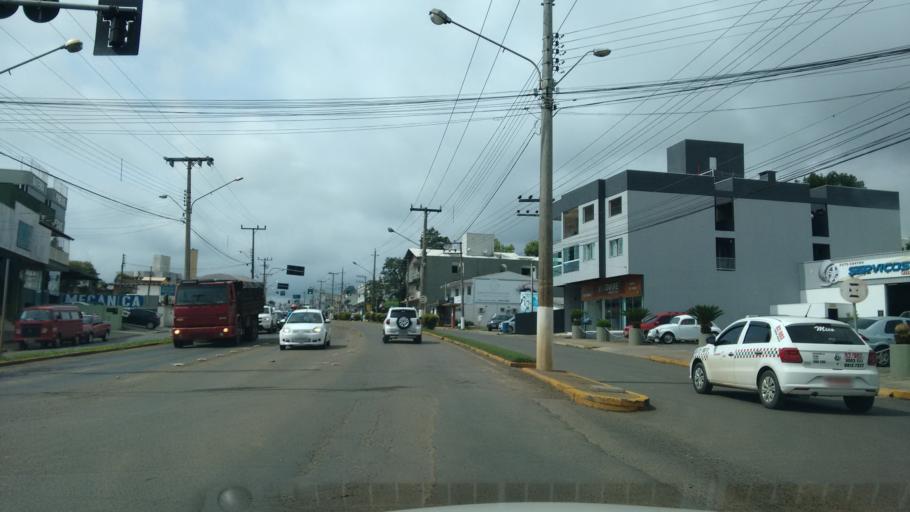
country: BR
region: Santa Catarina
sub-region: Videira
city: Videira
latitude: -27.0236
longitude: -50.9224
